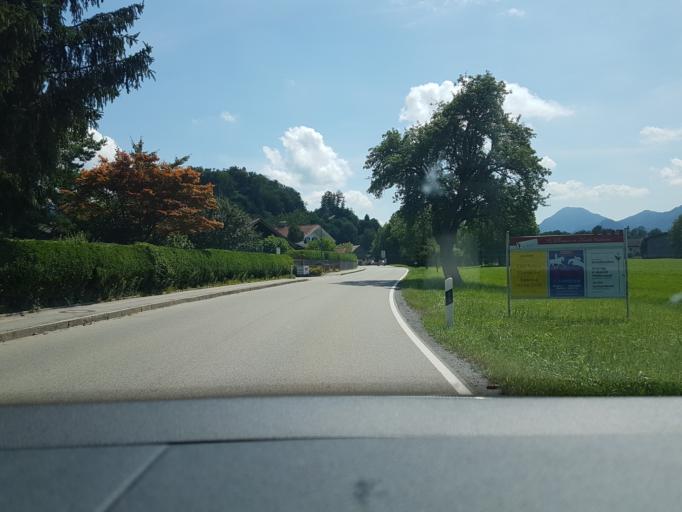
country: DE
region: Bavaria
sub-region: Upper Bavaria
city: Altenmarkt
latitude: 47.7817
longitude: 12.1332
